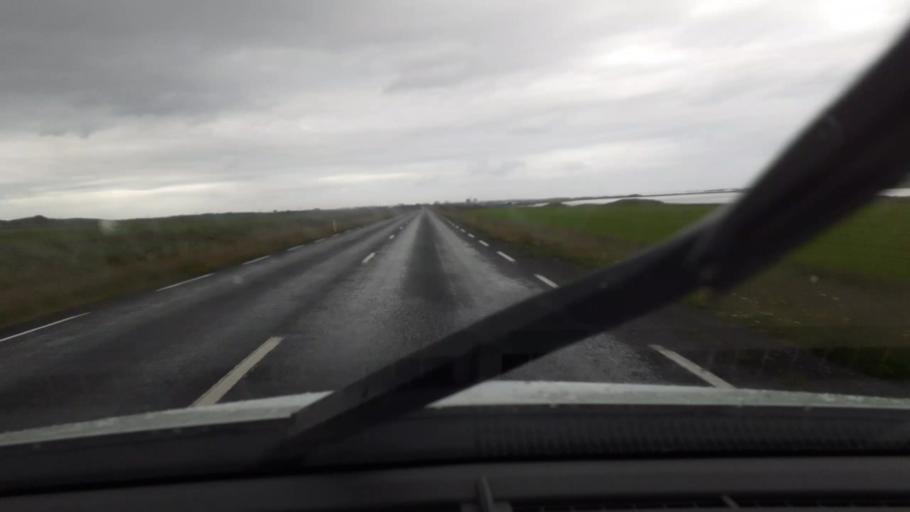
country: IS
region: West
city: Akranes
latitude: 64.3516
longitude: -21.9950
